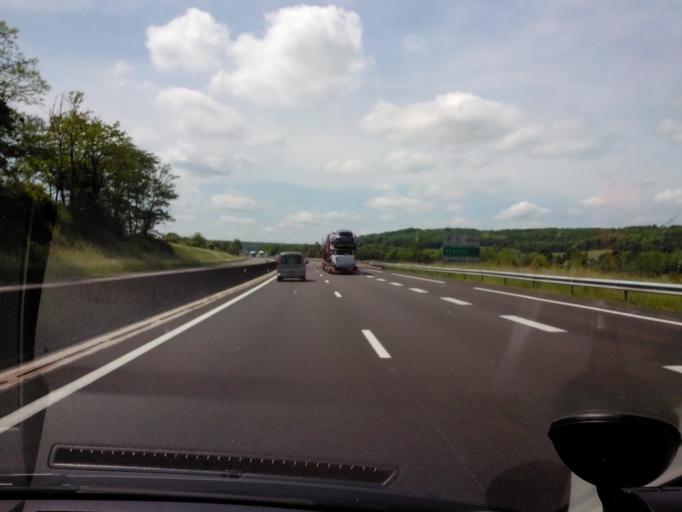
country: FR
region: Champagne-Ardenne
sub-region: Departement de la Haute-Marne
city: Rolampont
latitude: 47.9408
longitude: 5.2977
